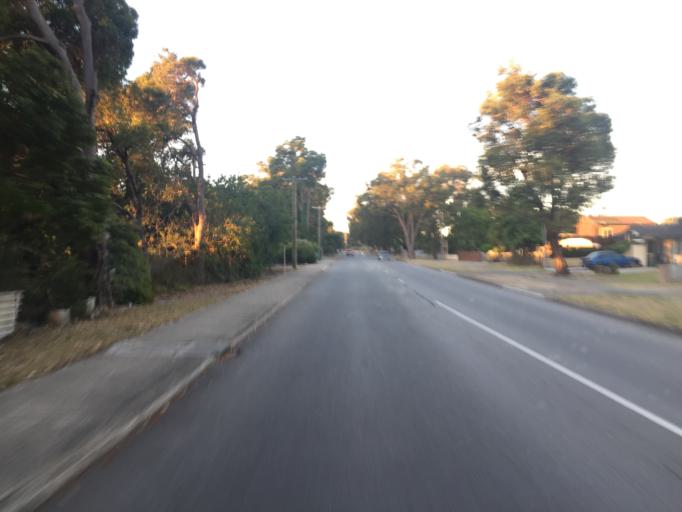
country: AU
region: Western Australia
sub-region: Gosnells
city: Kenwick
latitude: -32.0315
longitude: 115.9822
